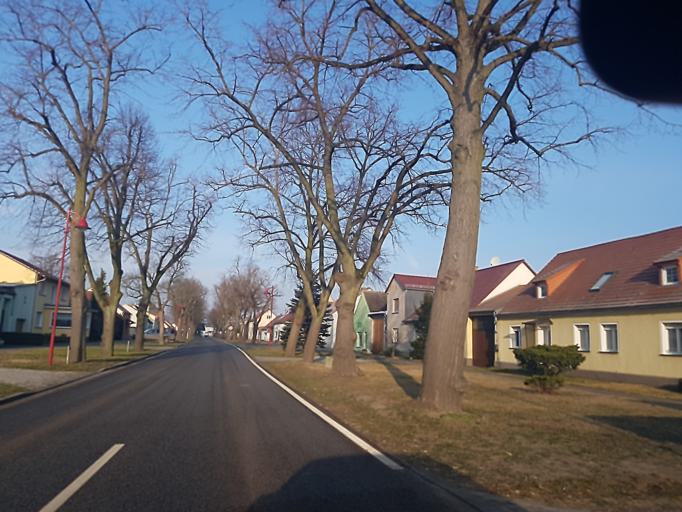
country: DE
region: Brandenburg
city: Golzow
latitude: 52.2575
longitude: 12.6636
